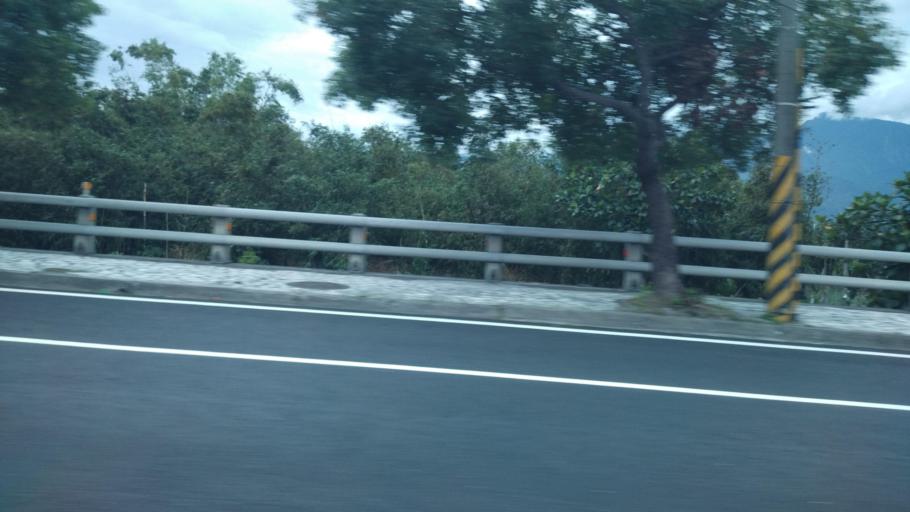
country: TW
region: Taiwan
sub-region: Hualien
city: Hualian
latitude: 24.0082
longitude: 121.6094
